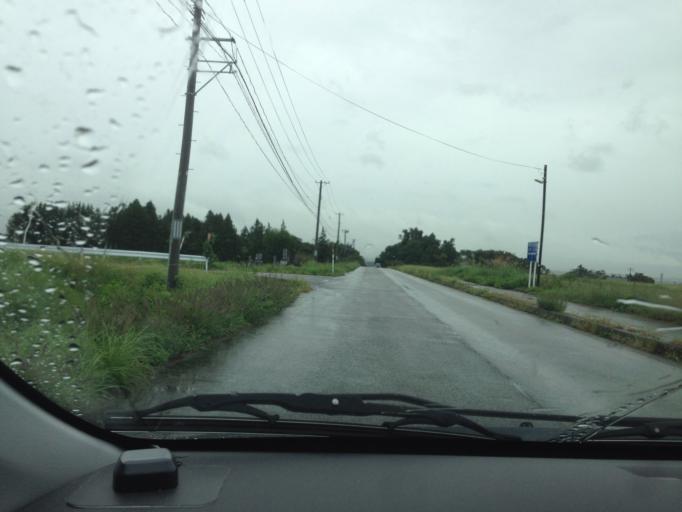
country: JP
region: Fukushima
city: Kitakata
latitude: 37.5113
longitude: 139.8168
